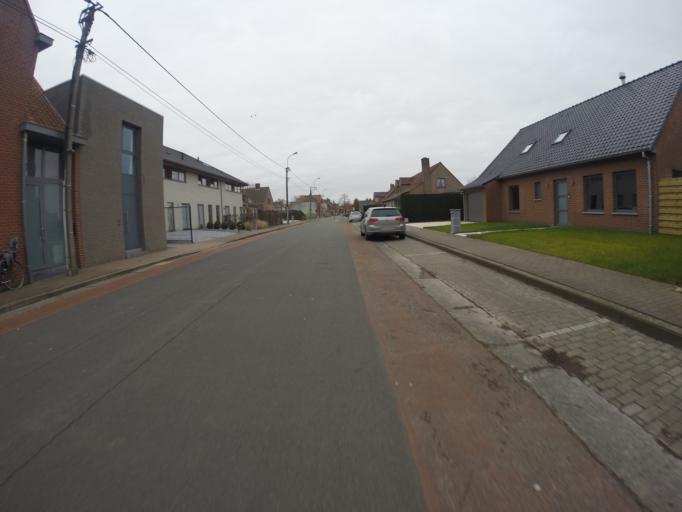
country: BE
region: Flanders
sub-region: Provincie Oost-Vlaanderen
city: Aalter
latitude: 51.1272
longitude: 3.4816
